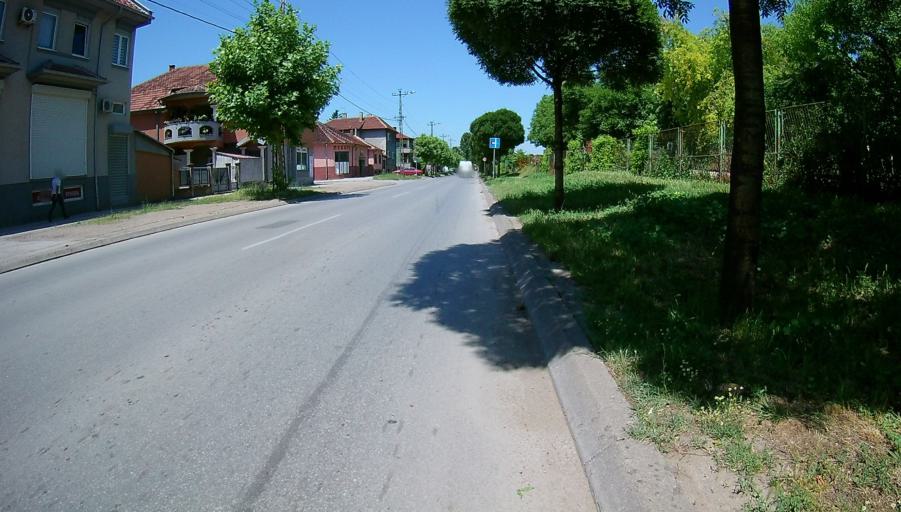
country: RS
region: Central Serbia
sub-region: Nisavski Okrug
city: Nis
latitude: 43.3141
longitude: 21.8864
